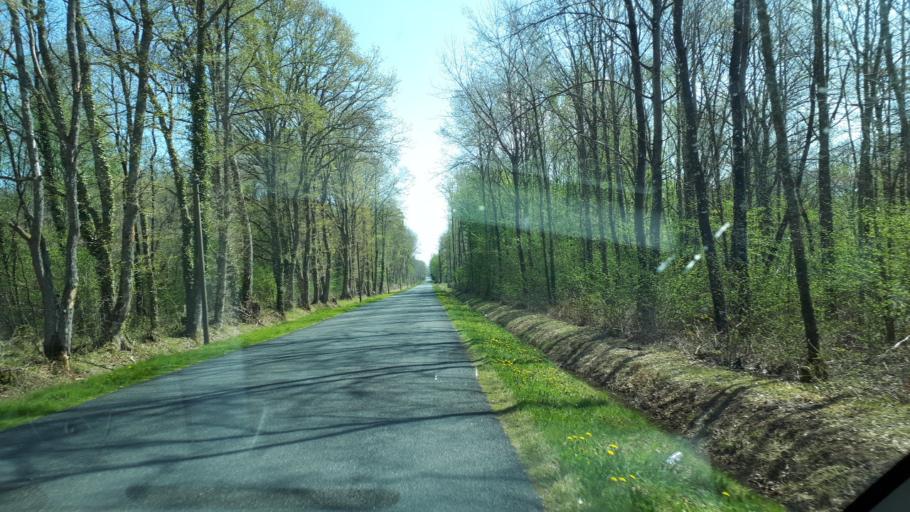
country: FR
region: Centre
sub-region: Departement du Cher
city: Neuvy-sur-Barangeon
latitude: 47.3172
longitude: 2.2344
